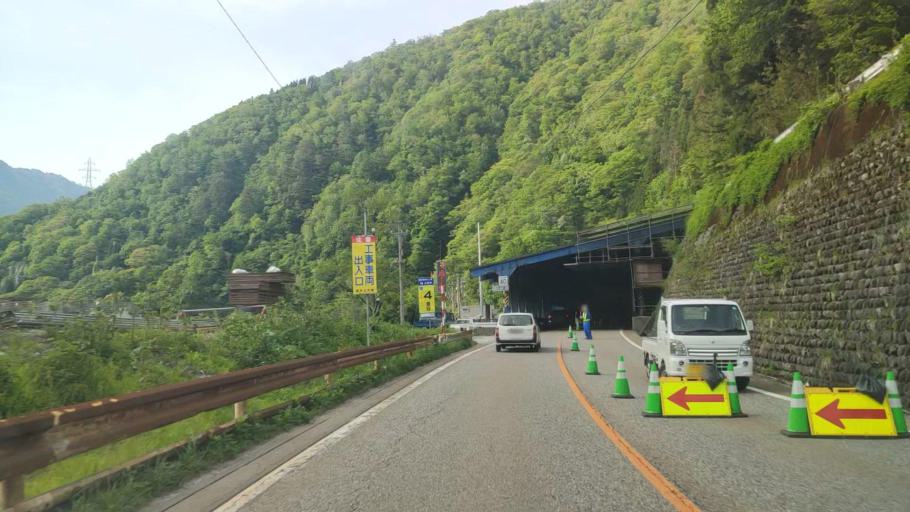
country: JP
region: Gifu
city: Takayama
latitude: 36.3692
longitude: 137.2826
